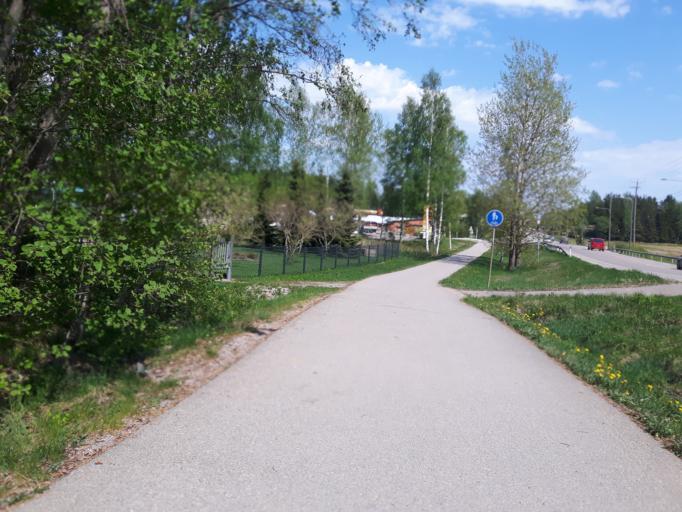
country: FI
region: Uusimaa
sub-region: Porvoo
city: Porvoo
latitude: 60.3784
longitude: 25.6105
